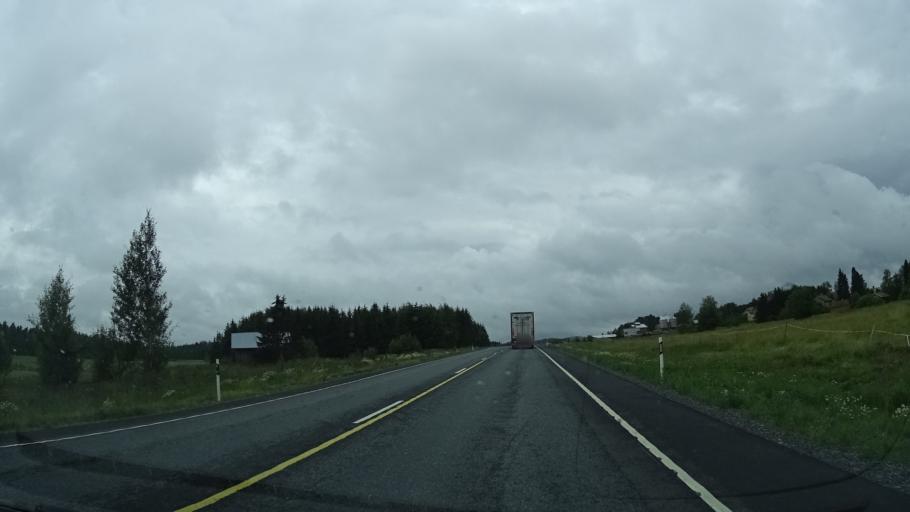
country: FI
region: Haeme
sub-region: Forssa
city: Tammela
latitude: 60.7573
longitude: 23.7019
